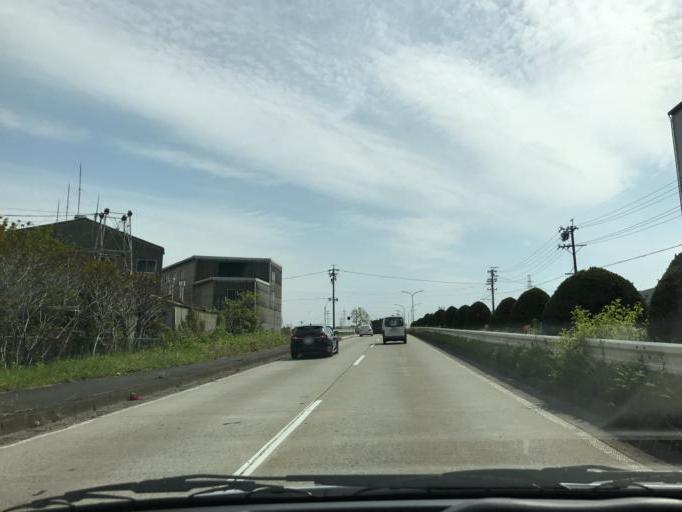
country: JP
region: Aichi
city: Obu
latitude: 35.0593
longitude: 136.9041
